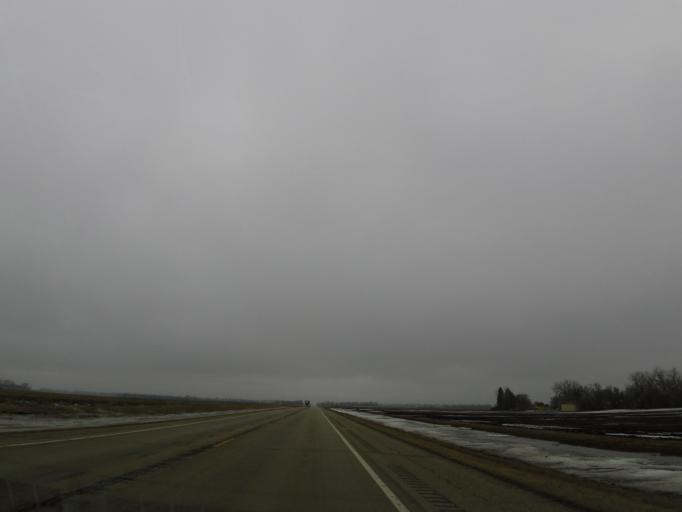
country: US
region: North Dakota
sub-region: Walsh County
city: Grafton
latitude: 48.5617
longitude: -97.4481
